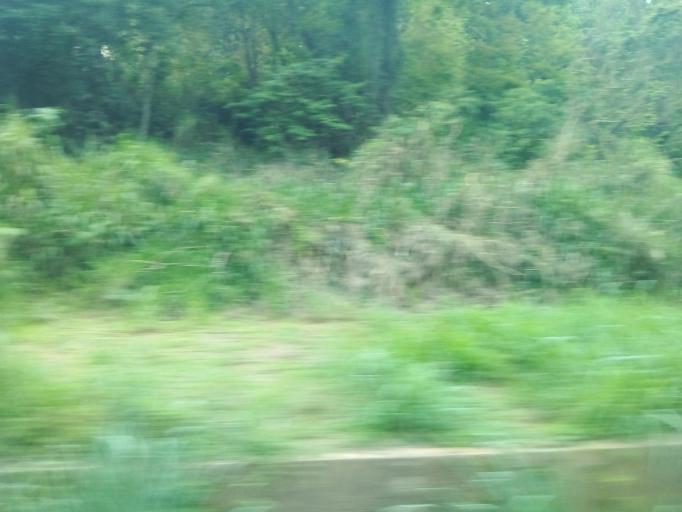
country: BR
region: Minas Gerais
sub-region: Nova Era
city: Nova Era
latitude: -19.7293
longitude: -43.0129
